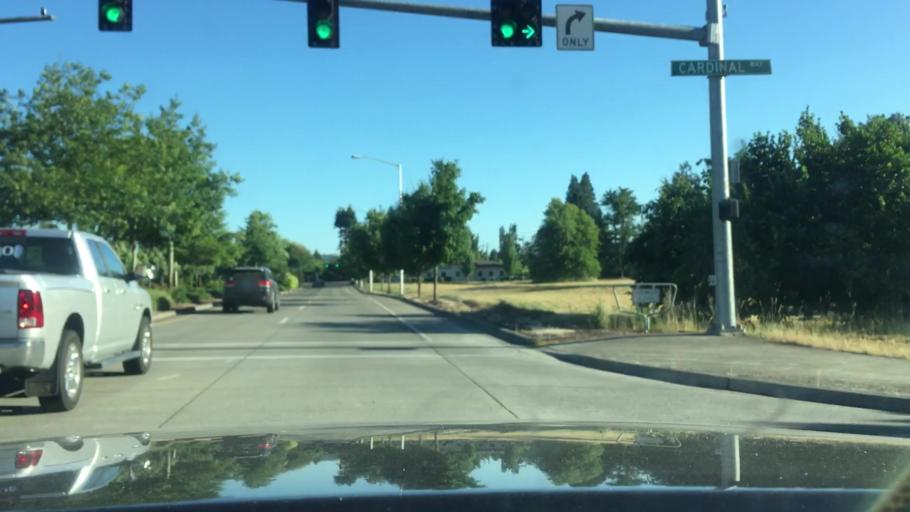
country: US
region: Oregon
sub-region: Lane County
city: Springfield
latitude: 44.0806
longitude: -123.0309
